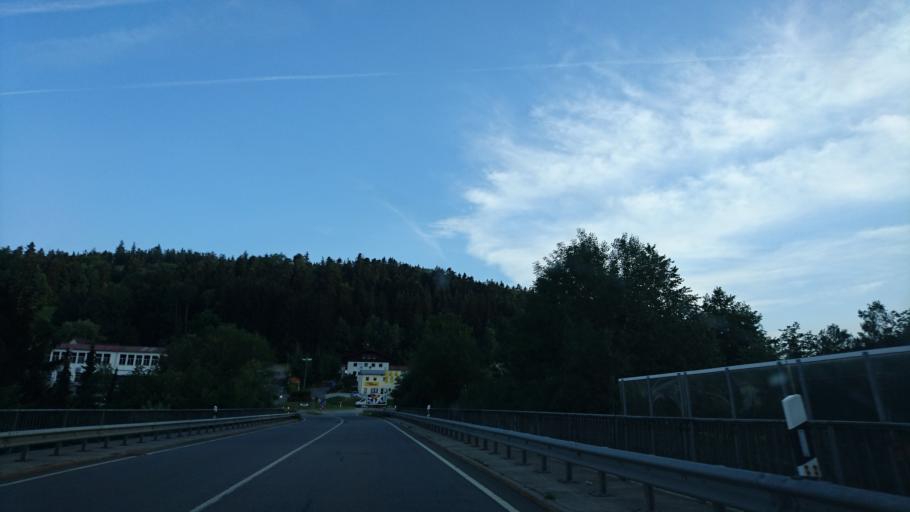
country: DE
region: Bavaria
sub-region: Lower Bavaria
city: Grafenau
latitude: 48.8580
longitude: 13.3849
